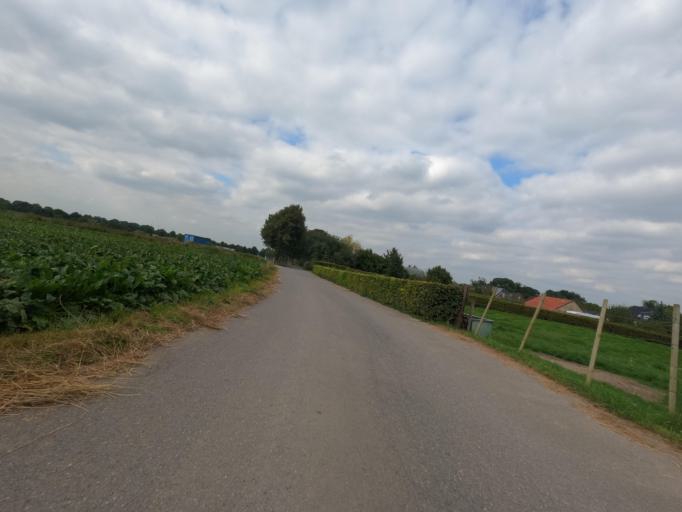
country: DE
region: North Rhine-Westphalia
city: Geilenkirchen
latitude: 50.9839
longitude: 6.1838
